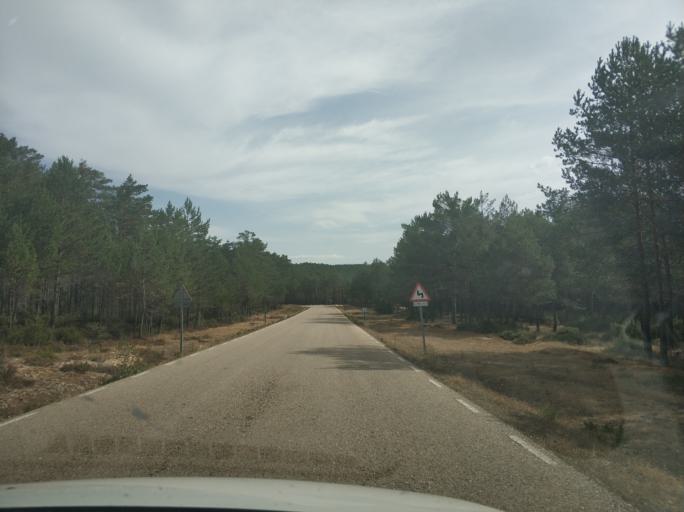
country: ES
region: Castille and Leon
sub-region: Provincia de Soria
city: Navaleno
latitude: 41.8541
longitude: -2.9748
